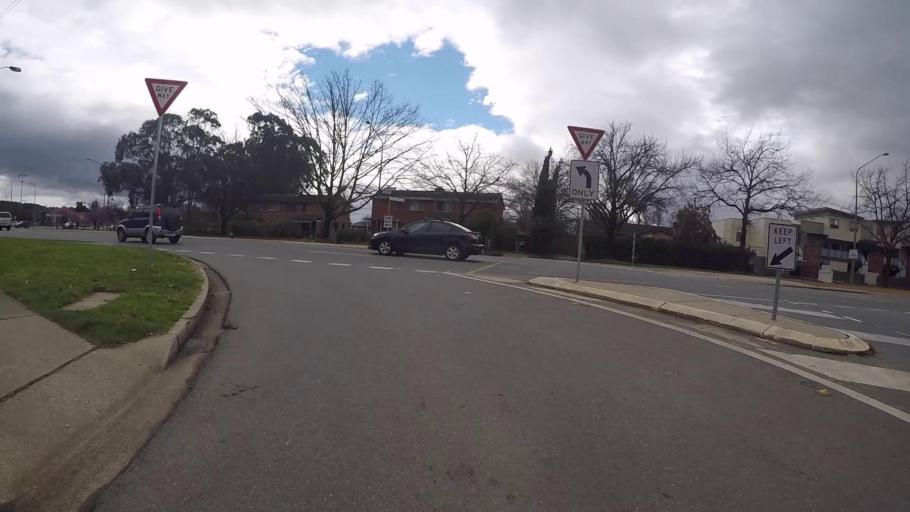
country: AU
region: Australian Capital Territory
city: Acton
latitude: -35.2485
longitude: 149.1357
